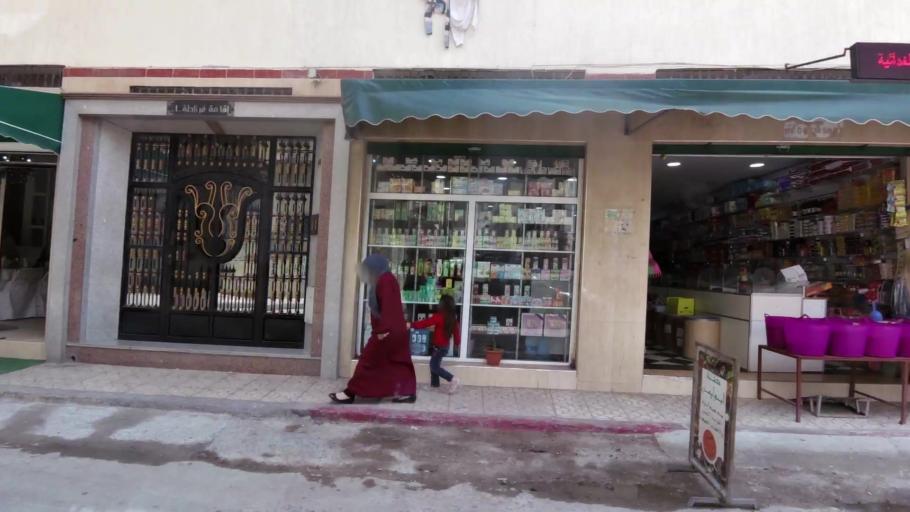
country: MA
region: Tanger-Tetouan
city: Tetouan
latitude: 35.5767
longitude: -5.3523
